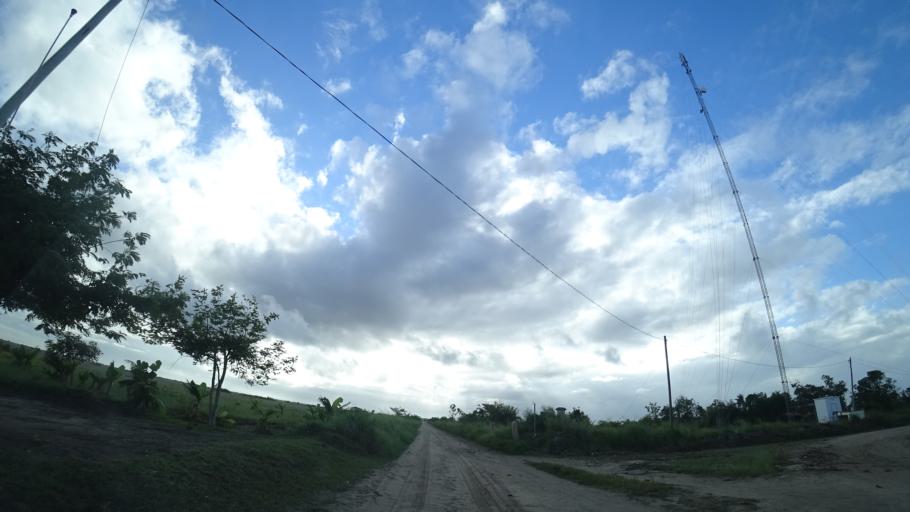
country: MZ
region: Sofala
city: Beira
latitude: -19.7134
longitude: 35.0119
